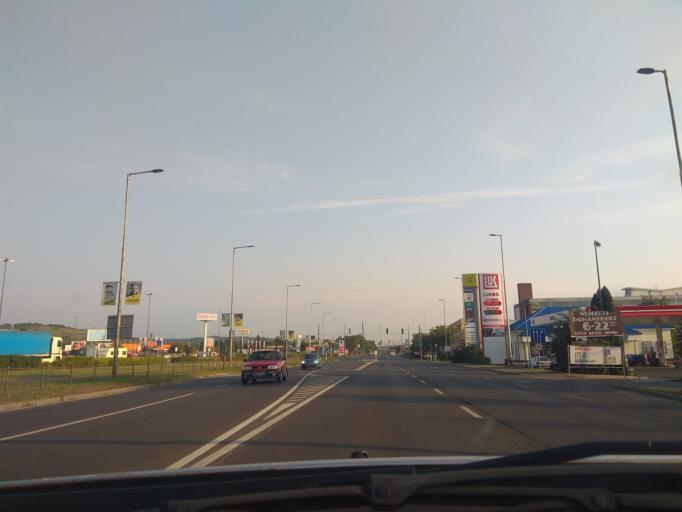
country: HU
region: Borsod-Abauj-Zemplen
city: Miskolc
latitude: 48.1260
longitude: 20.7849
